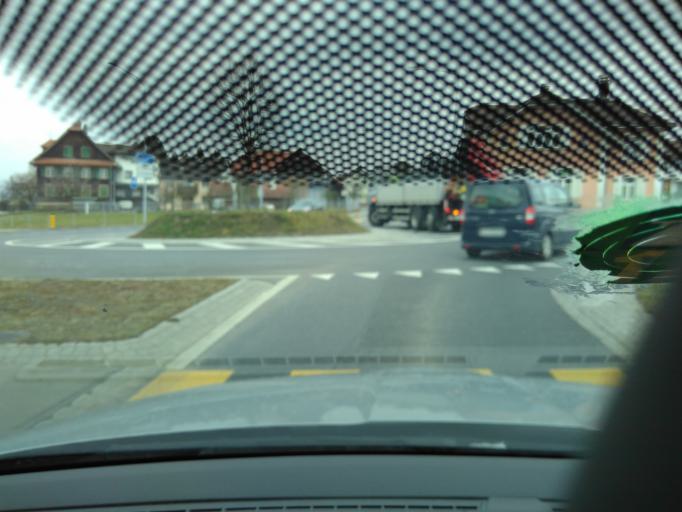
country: CH
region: Lucerne
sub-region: Hochdorf District
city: Hitzkirch
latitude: 47.2149
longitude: 8.2650
